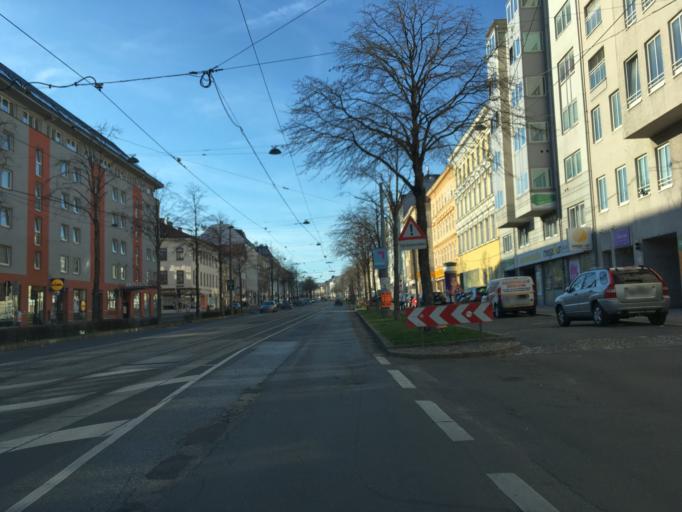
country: AT
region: Vienna
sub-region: Wien Stadt
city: Vienna
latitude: 48.2195
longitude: 16.3265
